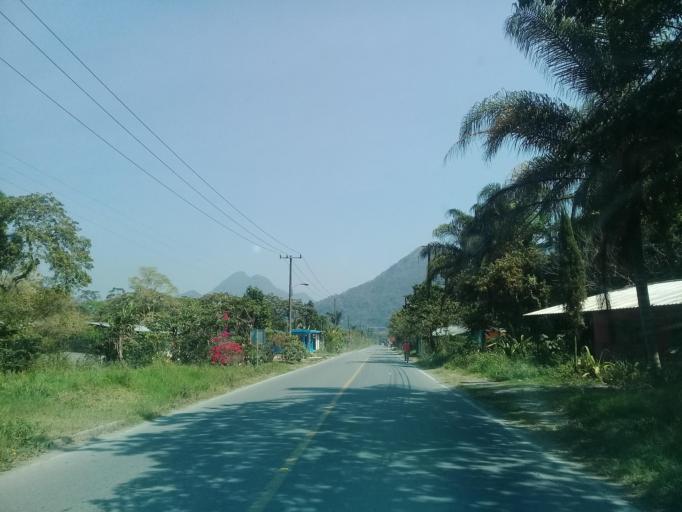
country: MX
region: Veracruz
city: Rafael Delgado
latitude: 18.7912
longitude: -97.0082
